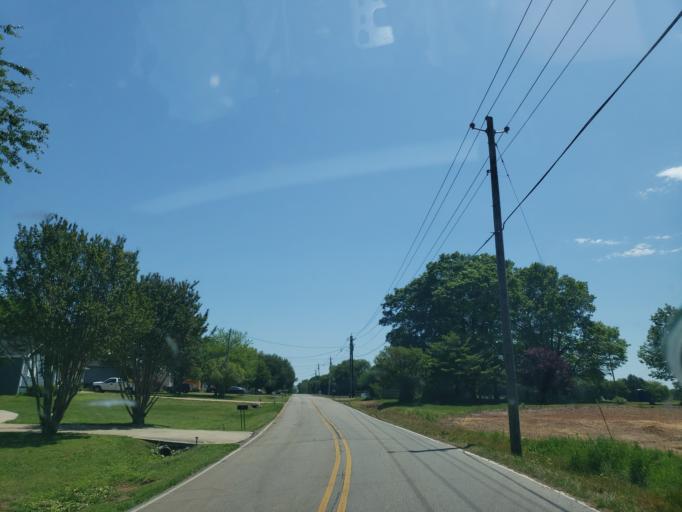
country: US
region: Alabama
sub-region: Madison County
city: Hazel Green
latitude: 34.9577
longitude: -86.5397
